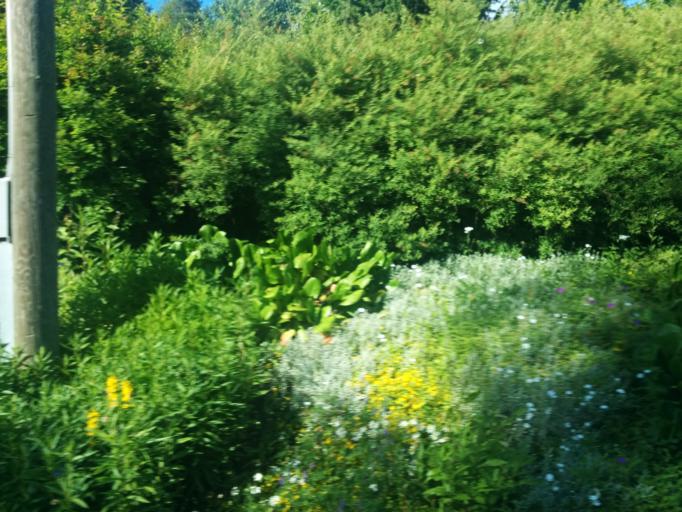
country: FI
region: Pirkanmaa
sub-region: Tampere
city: Tampere
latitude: 61.5010
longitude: 23.8576
